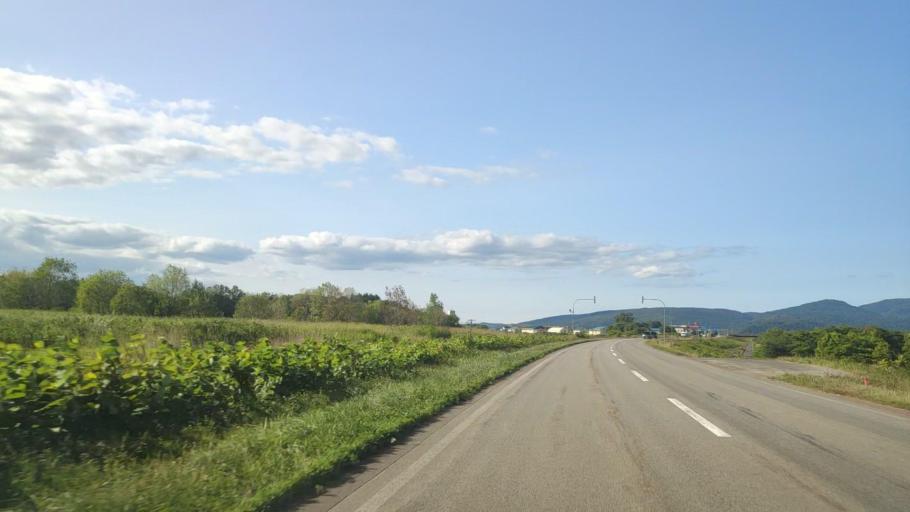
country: JP
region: Hokkaido
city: Nayoro
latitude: 44.8117
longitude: 142.0659
